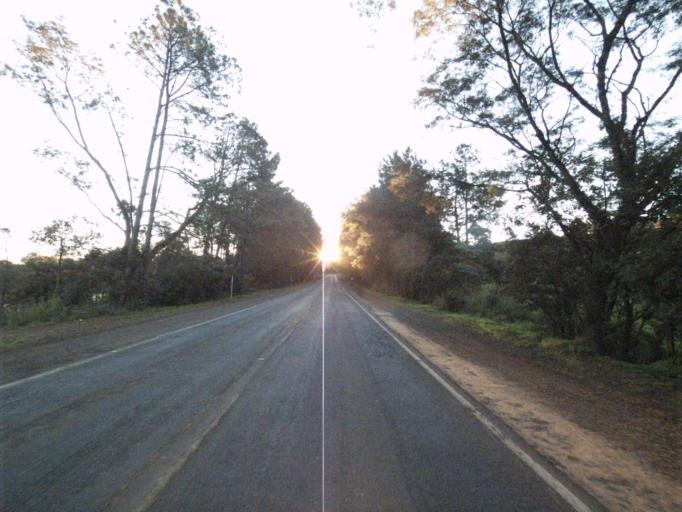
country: BR
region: Santa Catarina
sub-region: Sao Lourenco Do Oeste
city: Sao Lourenco dOeste
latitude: -26.8040
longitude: -53.1858
